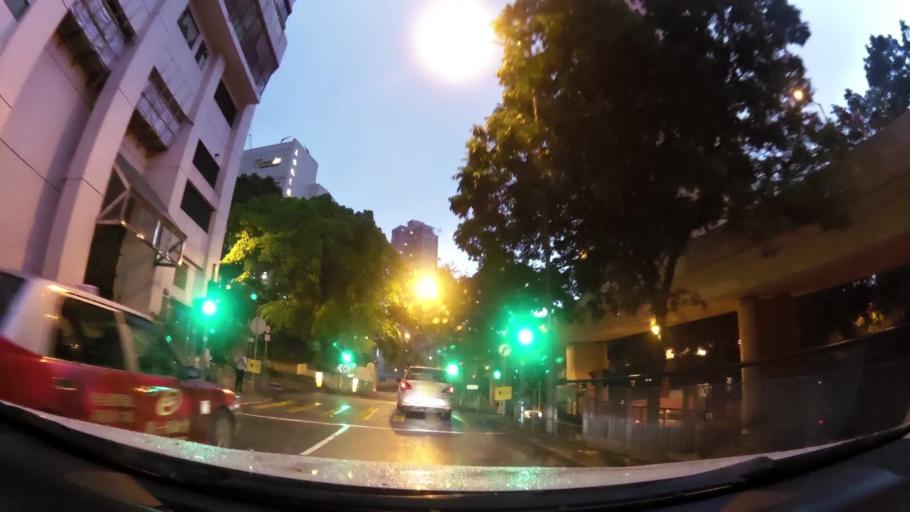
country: HK
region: Central and Western
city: Central
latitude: 22.2770
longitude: 114.1548
